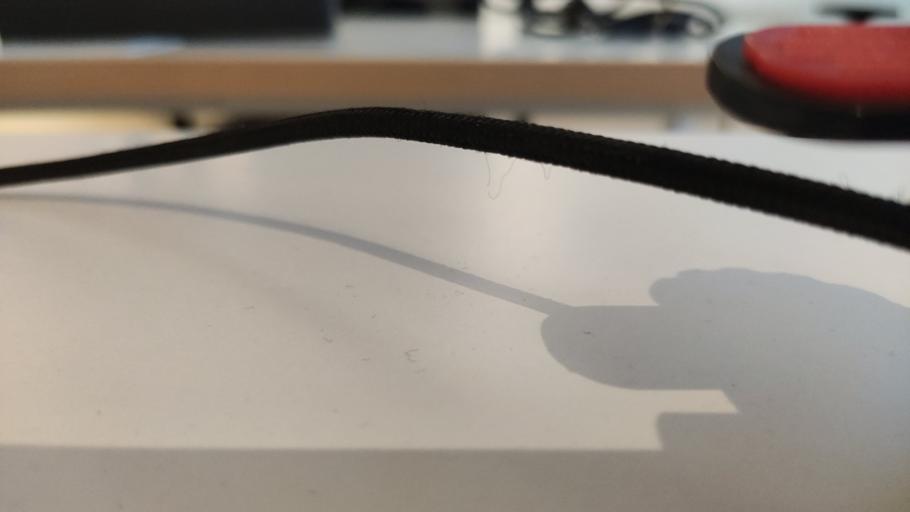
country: RU
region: Moskovskaya
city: Sychevo
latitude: 55.8348
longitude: 36.3270
